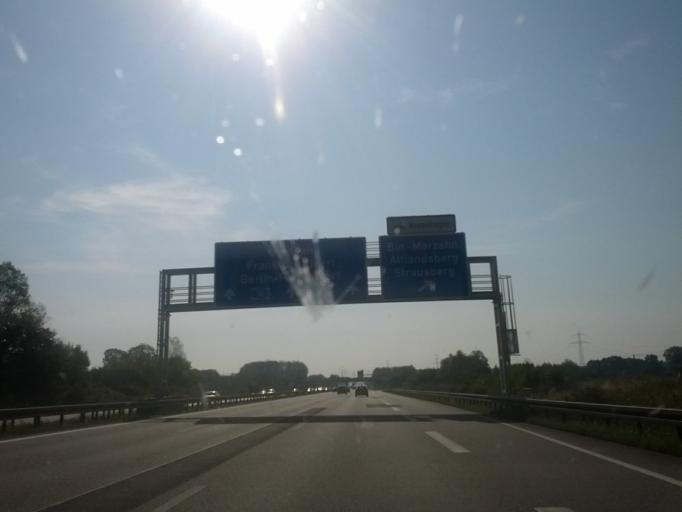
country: DE
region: Brandenburg
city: Neuenhagen
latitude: 52.5542
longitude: 13.6711
